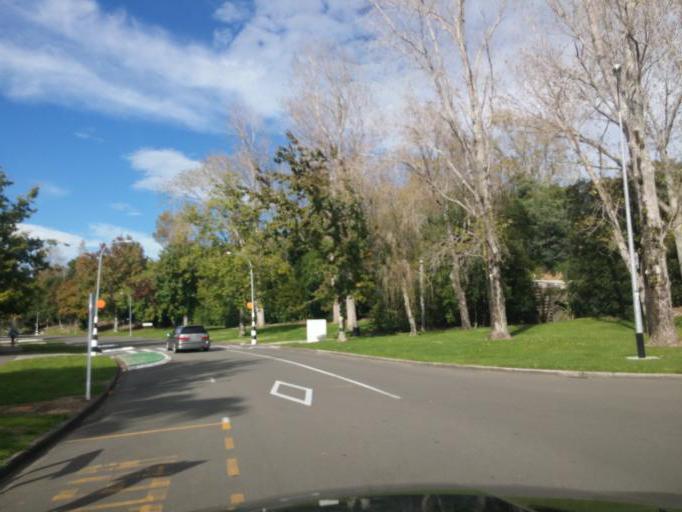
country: NZ
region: Manawatu-Wanganui
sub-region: Palmerston North City
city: Palmerston North
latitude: -40.3860
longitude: 175.6148
